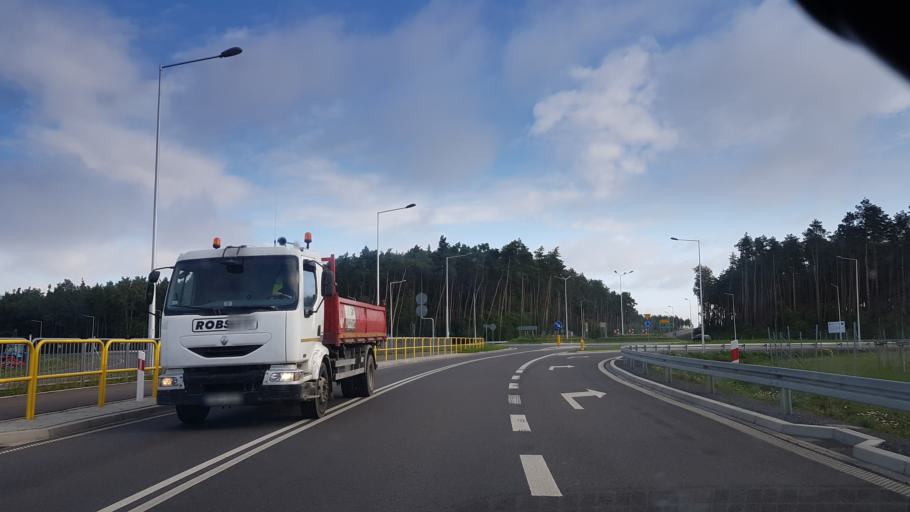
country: PL
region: Greater Poland Voivodeship
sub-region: Leszno
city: Leszno
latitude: 51.8108
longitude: 16.5870
